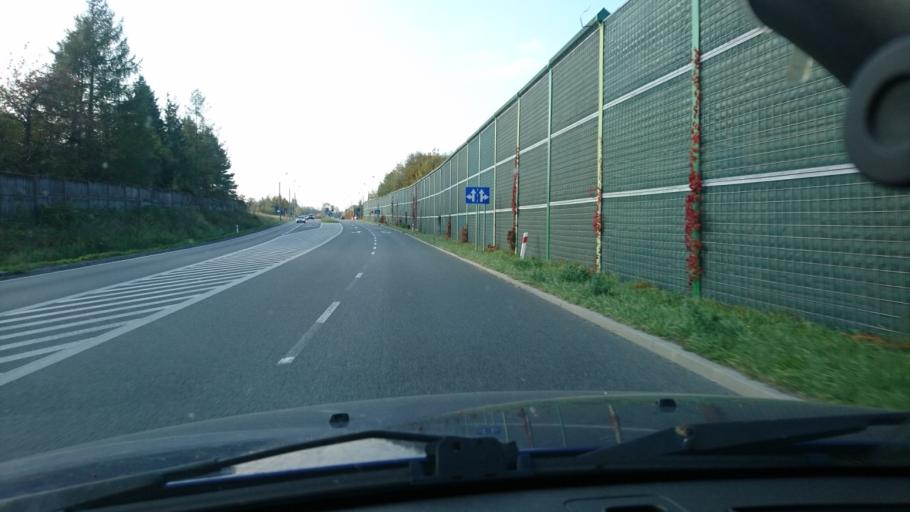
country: PL
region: Silesian Voivodeship
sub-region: Powiat cieszynski
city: Ustron
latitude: 49.7157
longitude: 18.8041
